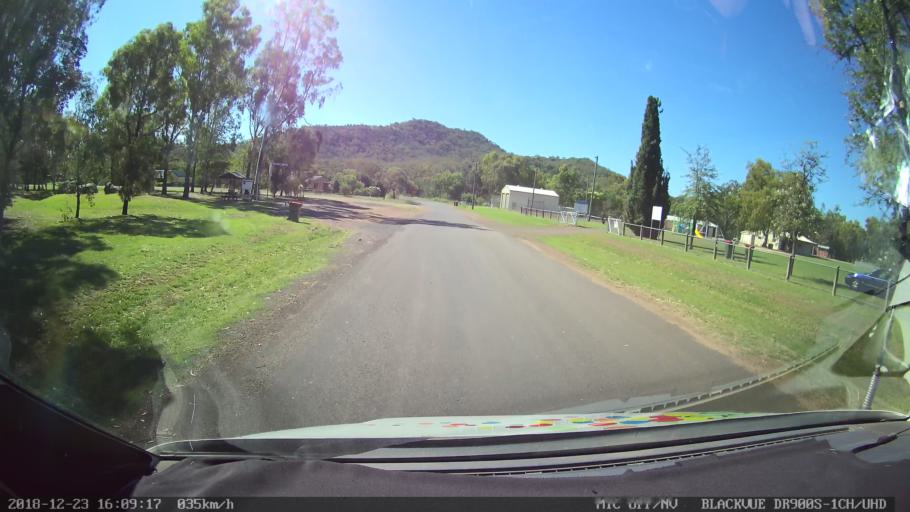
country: AU
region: New South Wales
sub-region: Tamworth Municipality
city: Phillip
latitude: -31.2615
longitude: 150.7396
